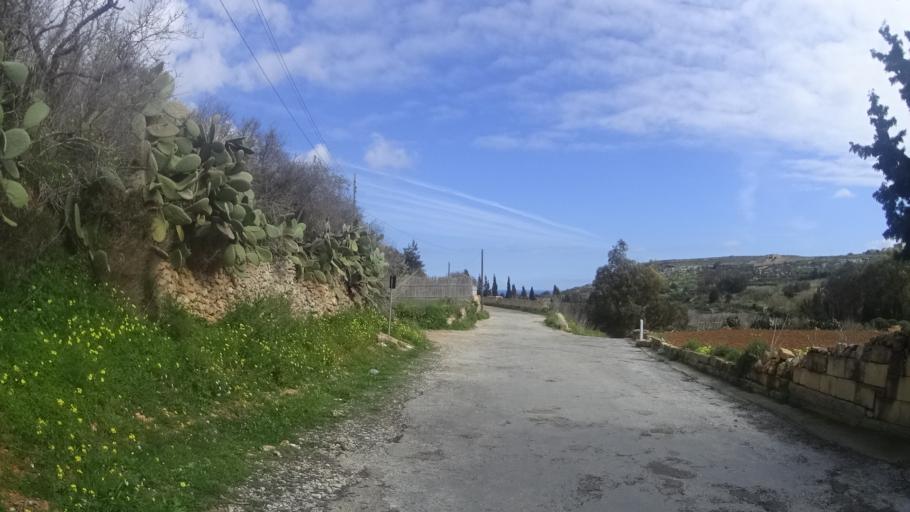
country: MT
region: Il-Qala
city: Qala
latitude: 36.0453
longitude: 14.3057
